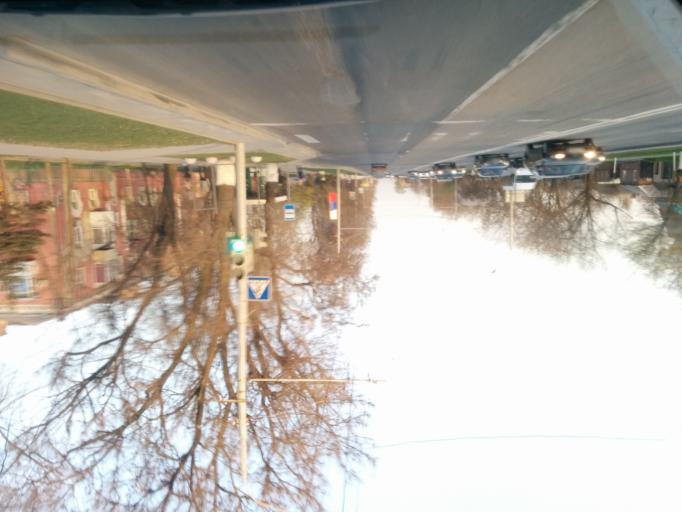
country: RU
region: Rostov
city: Imeni Chkalova
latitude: 47.2458
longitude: 39.7710
